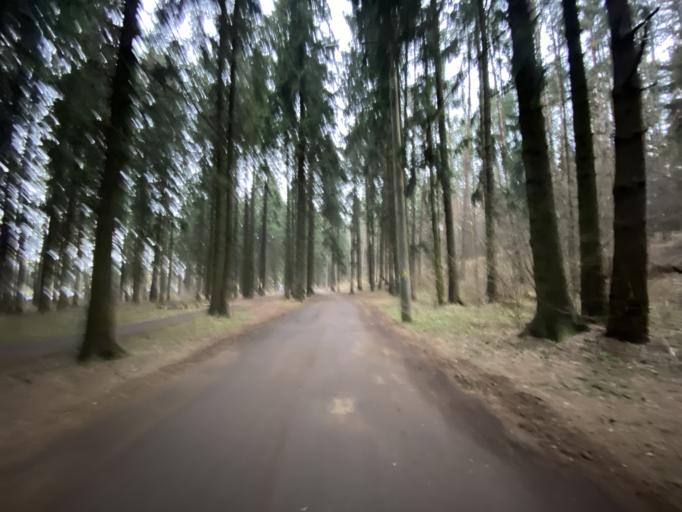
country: BY
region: Minsk
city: Borovlyany
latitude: 53.9461
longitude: 27.6521
